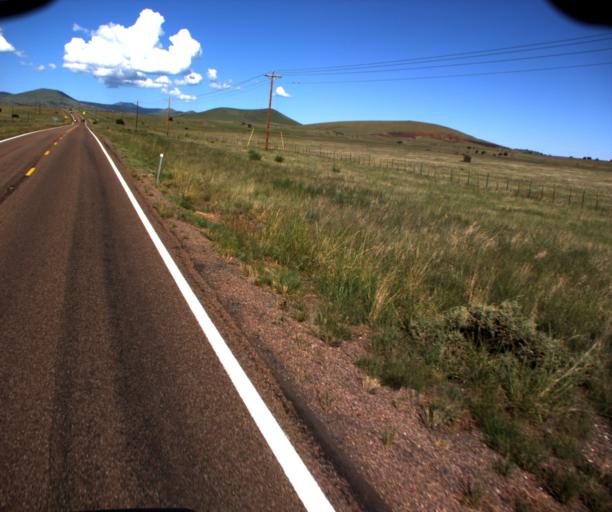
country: US
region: Arizona
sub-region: Apache County
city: Eagar
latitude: 34.1043
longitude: -109.3543
